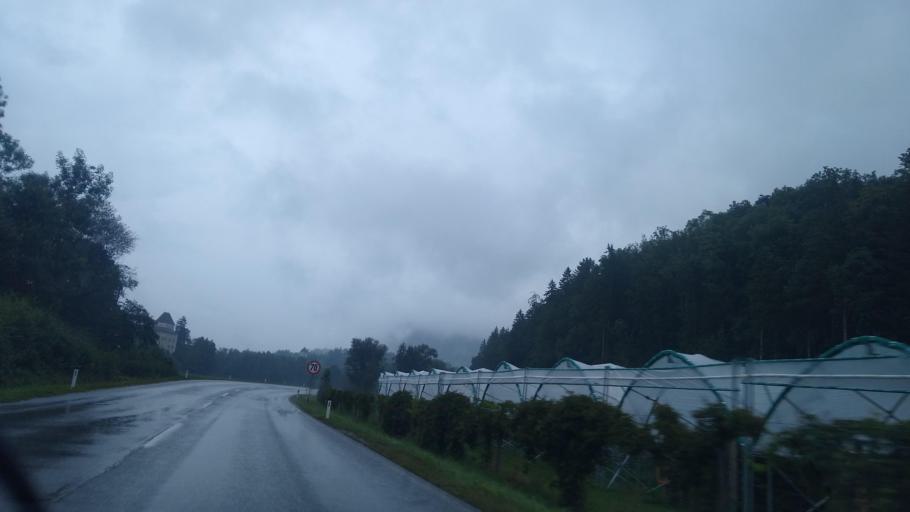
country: AT
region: Tyrol
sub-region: Politischer Bezirk Kufstein
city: Reith im Alpbachtal
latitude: 47.4158
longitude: 11.8564
